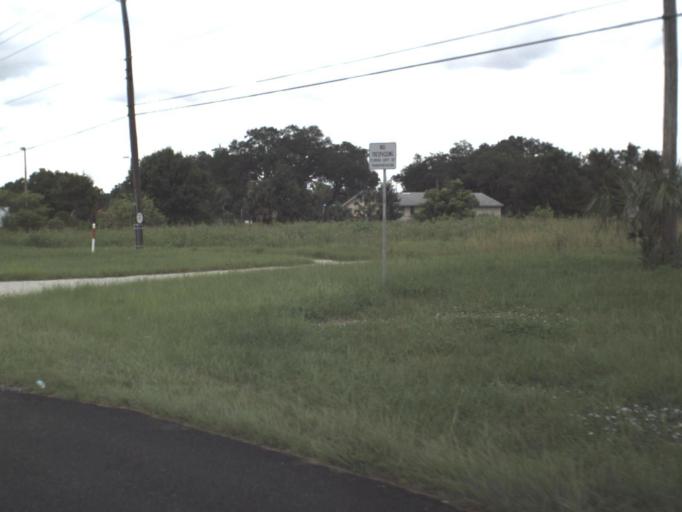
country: US
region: Florida
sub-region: Hillsborough County
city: East Lake-Orient Park
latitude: 27.9963
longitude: -82.3804
